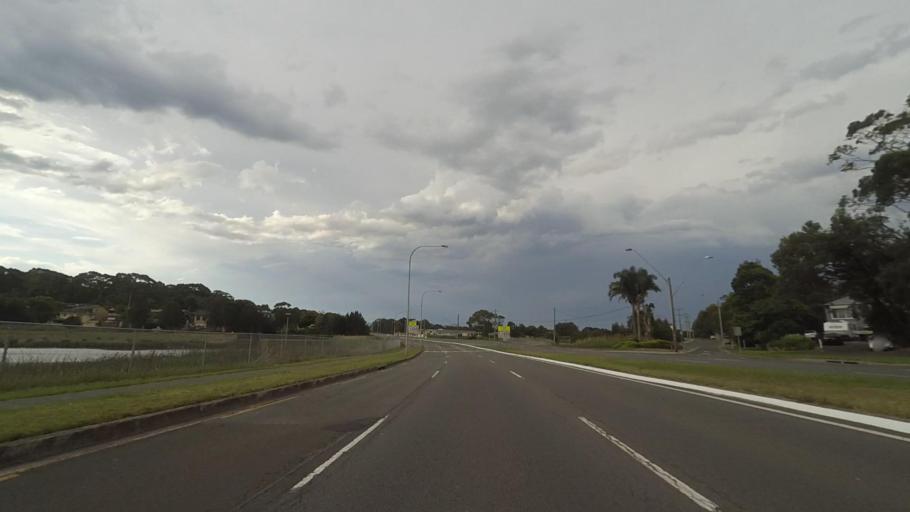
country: AU
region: New South Wales
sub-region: Shellharbour
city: Shellharbour Village
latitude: -34.5760
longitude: 150.8640
